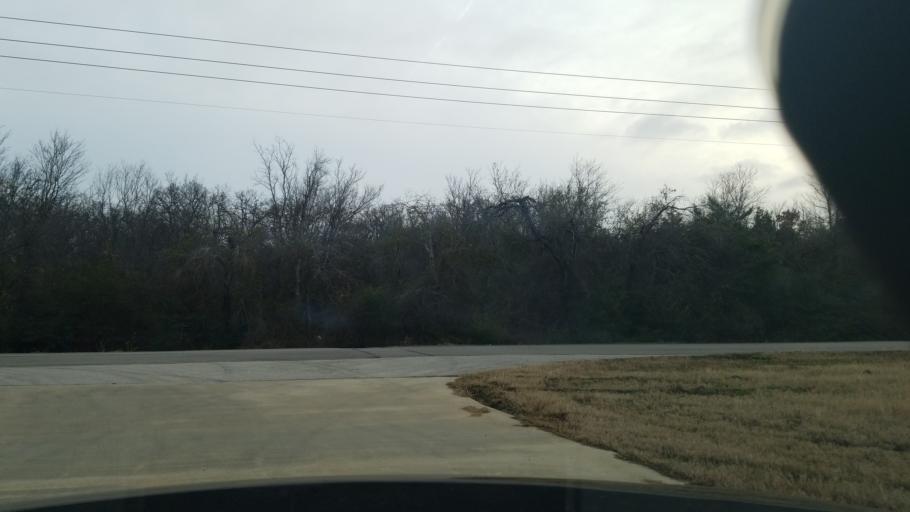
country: US
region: Texas
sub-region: Denton County
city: Corinth
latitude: 33.1448
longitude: -97.0497
